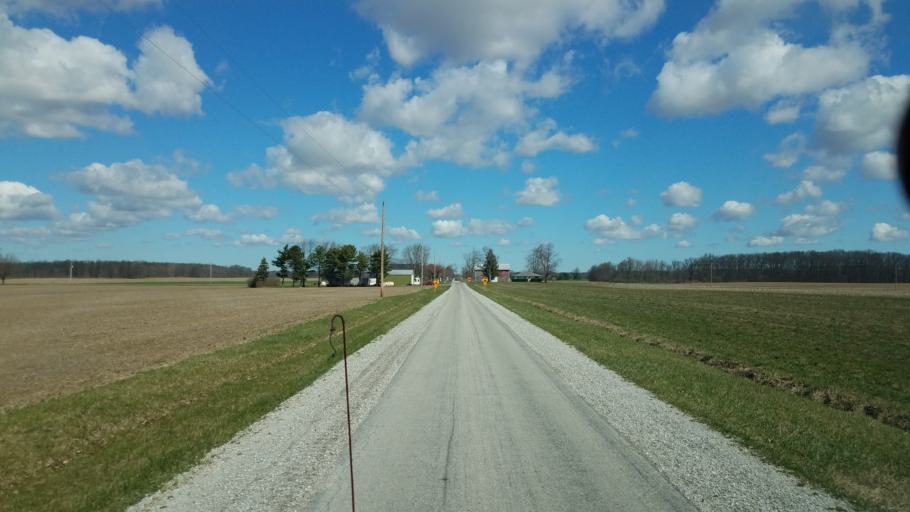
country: US
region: Ohio
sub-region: Sandusky County
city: Mount Carmel
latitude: 41.1072
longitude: -82.9383
